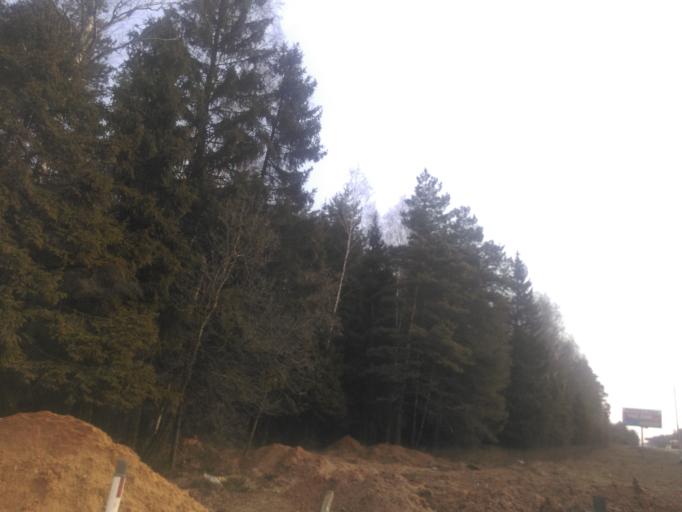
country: RU
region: Moskovskaya
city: Chupryakovo
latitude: 55.5617
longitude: 36.6069
